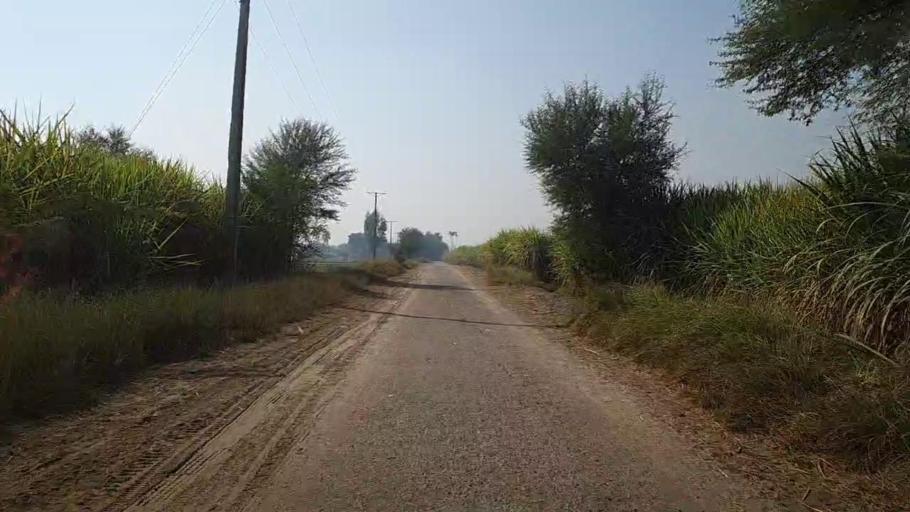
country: PK
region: Sindh
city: Bozdar
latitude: 27.2658
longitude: 68.6237
